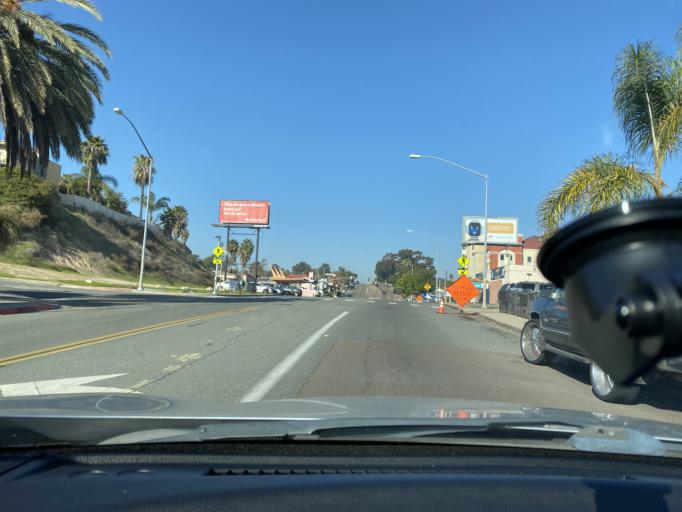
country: US
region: California
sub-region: San Diego County
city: National City
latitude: 32.7099
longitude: -117.0936
